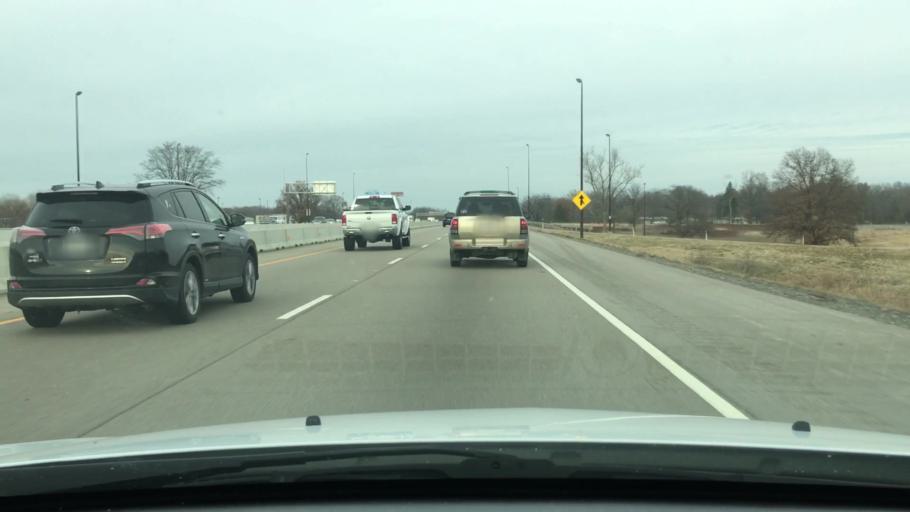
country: US
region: Illinois
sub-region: Sangamon County
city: Grandview
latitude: 39.7842
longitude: -89.5998
